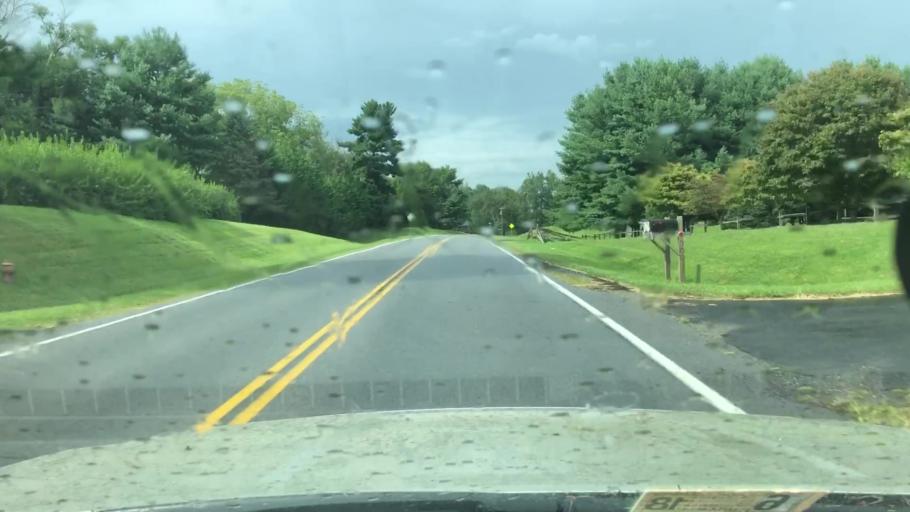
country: US
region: Virginia
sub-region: City of Waynesboro
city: Waynesboro
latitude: 38.0860
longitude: -78.9012
